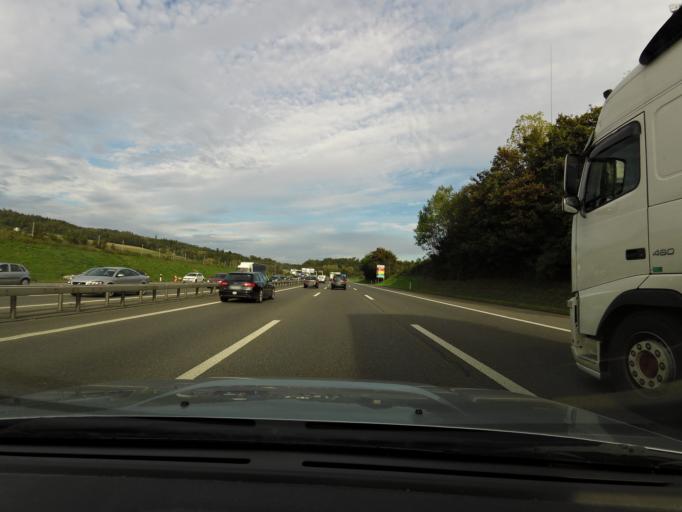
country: CH
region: Aargau
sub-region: Bezirk Baden
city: Birmenstorf
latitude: 47.4509
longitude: 8.2609
